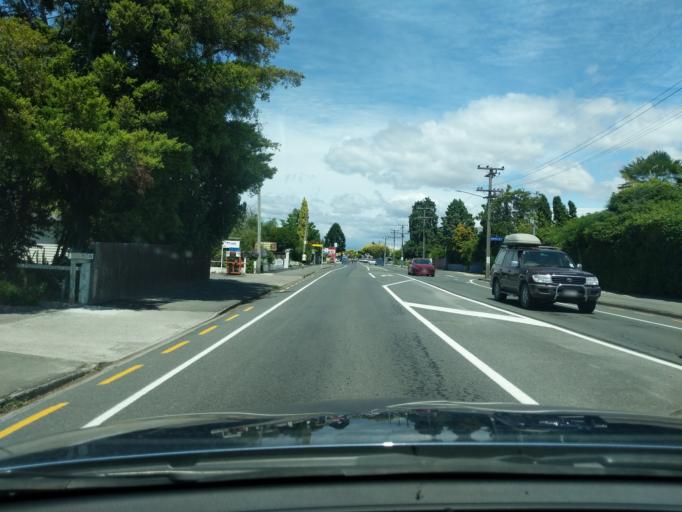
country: NZ
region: Tasman
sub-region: Tasman District
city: Motueka
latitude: -41.1061
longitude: 173.0114
